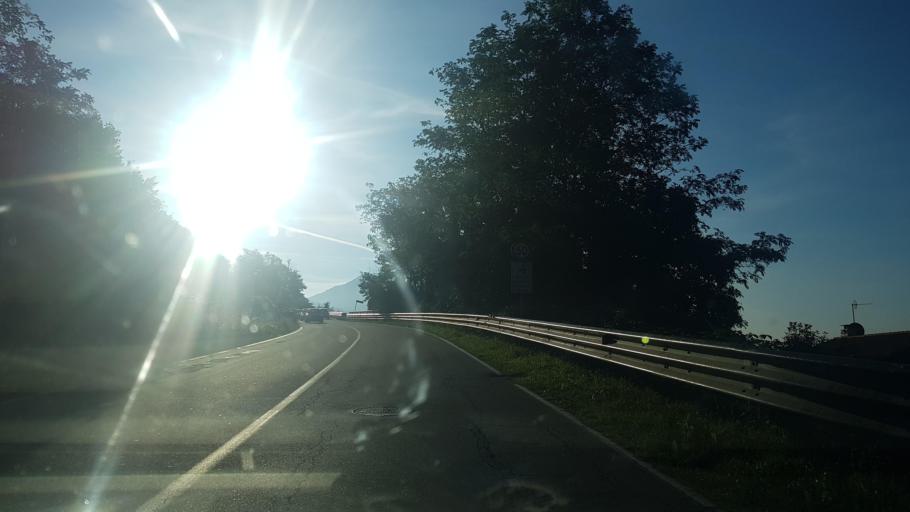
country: IT
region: Piedmont
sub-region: Provincia Verbano-Cusio-Ossola
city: Pallanza-Intra-Suna
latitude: 45.9442
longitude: 8.5679
